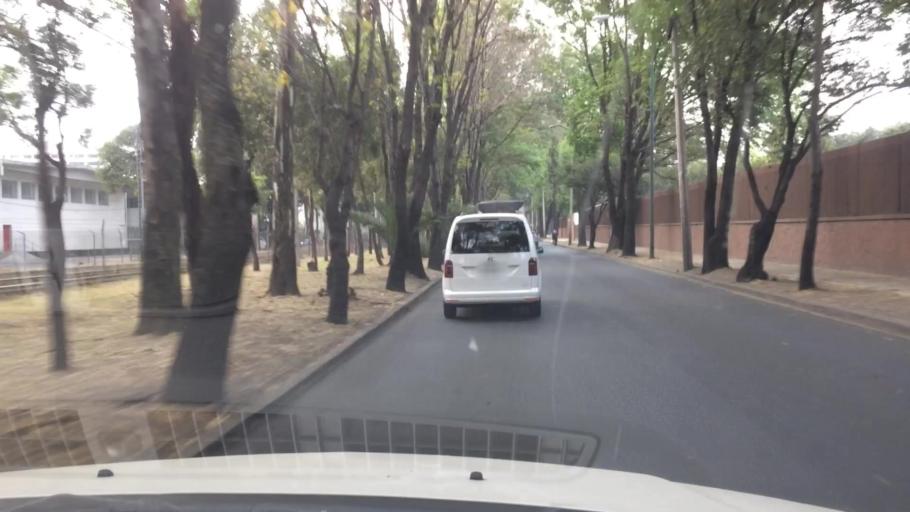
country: MX
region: Mexico City
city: Tlalpan
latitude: 19.2855
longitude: -99.1427
